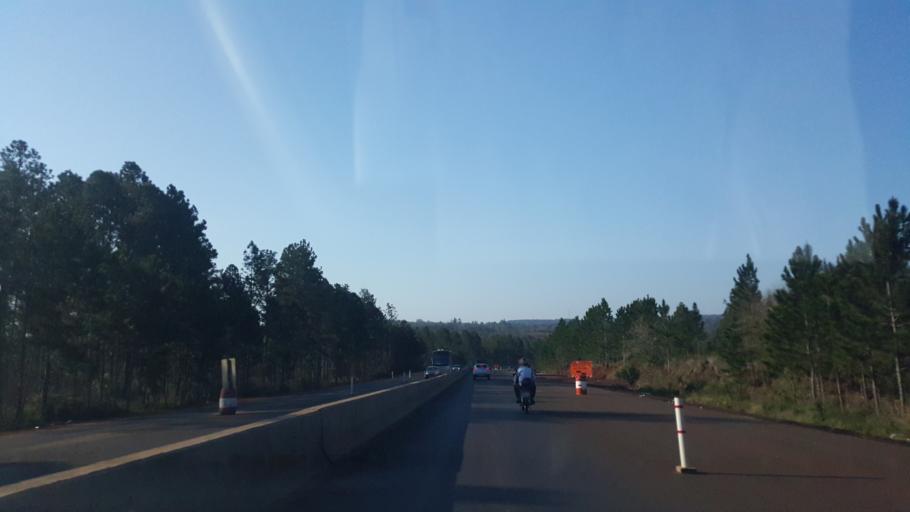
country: AR
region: Misiones
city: Santa Ana
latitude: -27.3934
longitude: -55.5992
